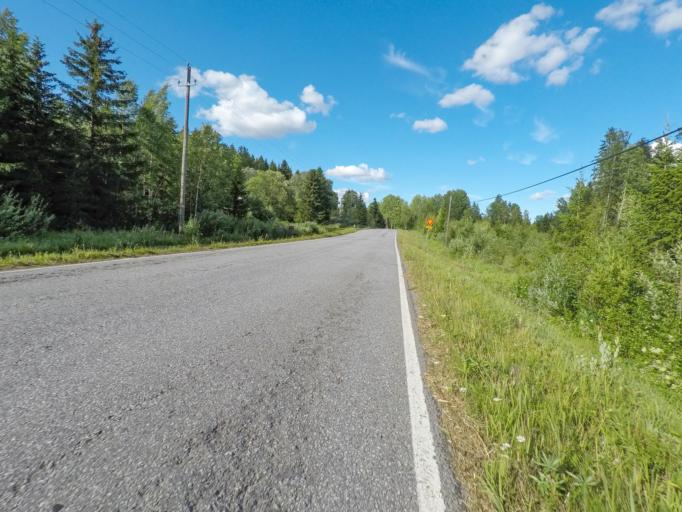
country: FI
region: South Karelia
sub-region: Imatra
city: Imatra
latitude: 61.1400
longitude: 28.7407
